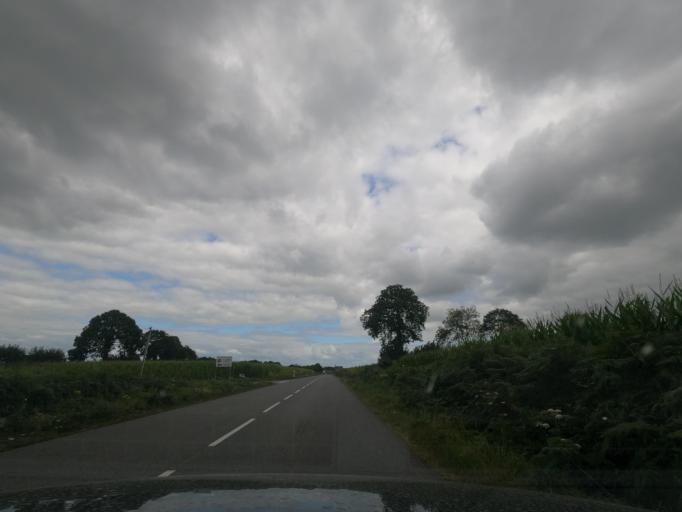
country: FR
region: Brittany
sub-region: Departement d'Ille-et-Vilaine
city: Landean
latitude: 48.4258
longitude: -1.1233
